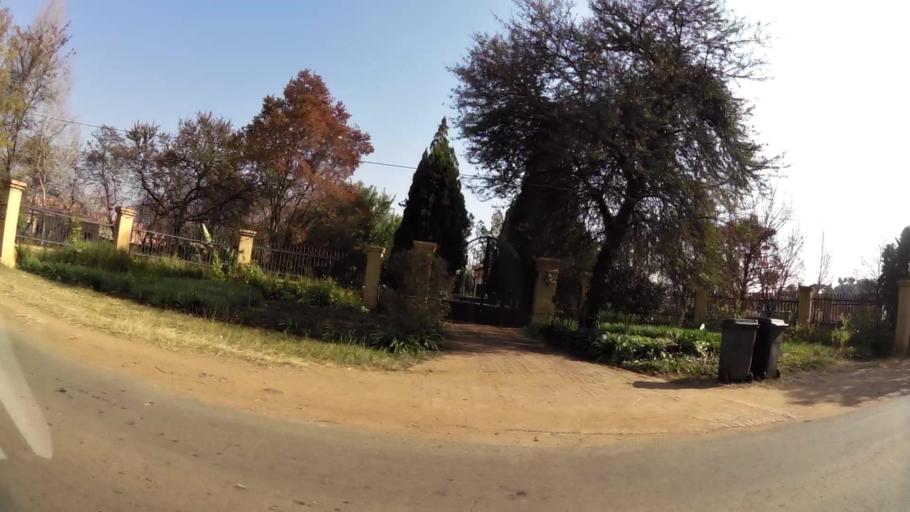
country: ZA
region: Gauteng
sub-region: City of Tshwane Metropolitan Municipality
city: Pretoria
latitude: -25.7709
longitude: 28.3501
